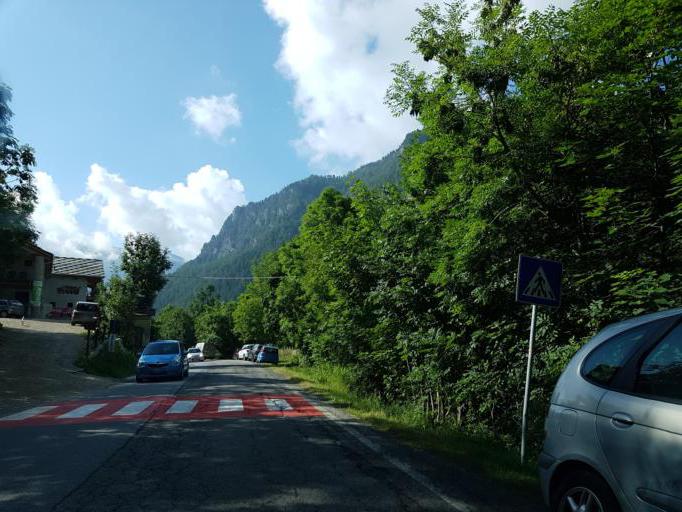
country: IT
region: Piedmont
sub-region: Provincia di Cuneo
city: Pontechianale
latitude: 44.6139
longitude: 7.0527
